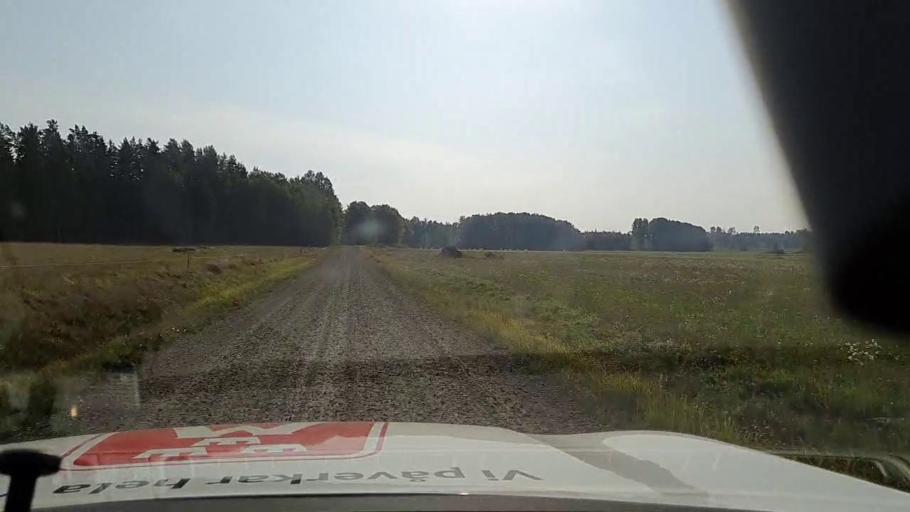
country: SE
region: Vaestmanland
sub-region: Kungsors Kommun
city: Kungsoer
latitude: 59.3520
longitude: 16.1625
